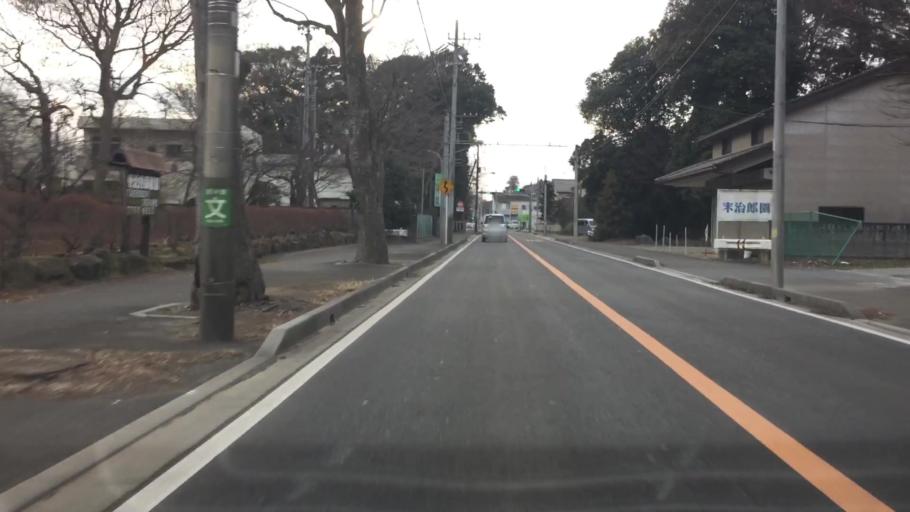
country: JP
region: Chiba
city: Matsudo
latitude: 35.7706
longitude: 139.9646
